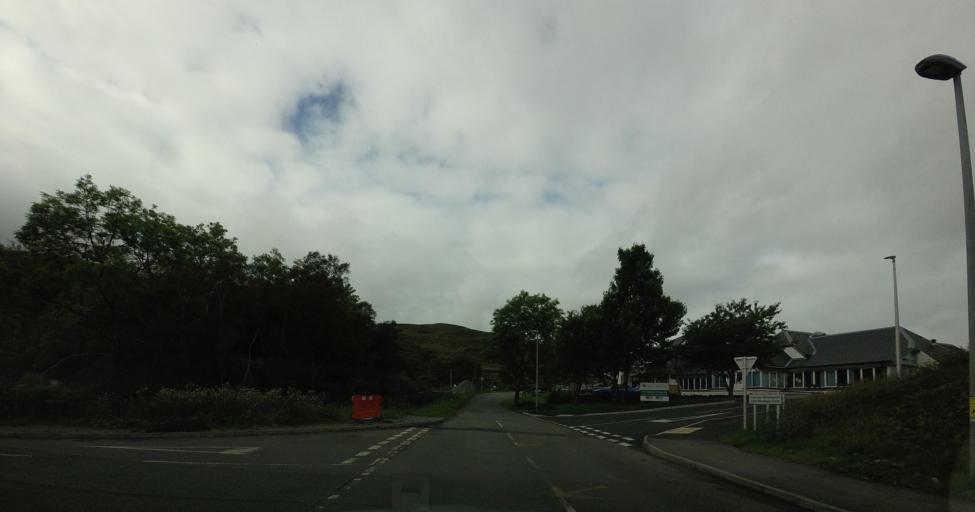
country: GB
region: Scotland
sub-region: Highland
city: Portree
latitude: 57.4138
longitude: -6.2110
